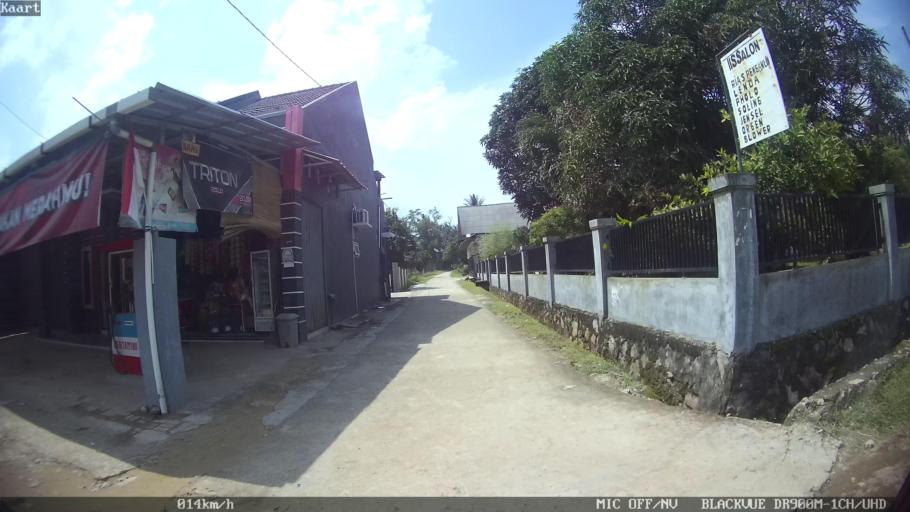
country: ID
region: Lampung
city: Kedaton
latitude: -5.3330
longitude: 105.3012
